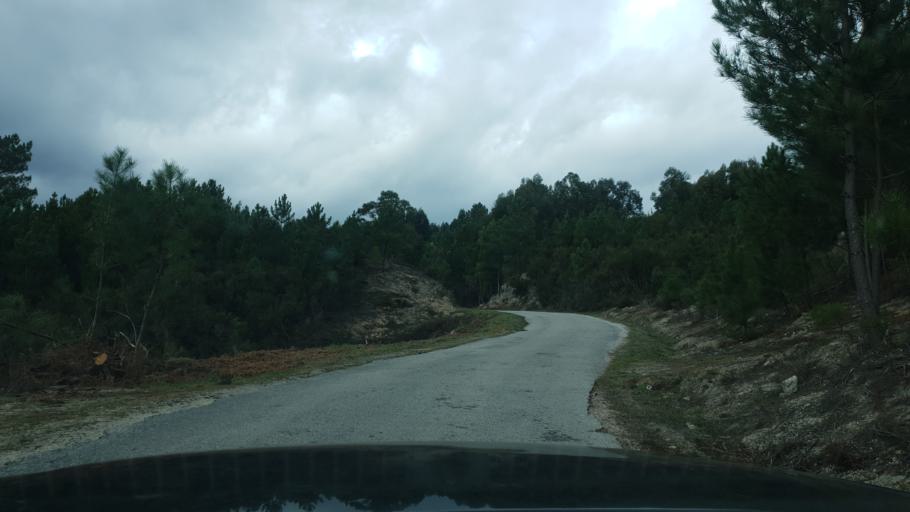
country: PT
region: Viseu
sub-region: Castro Daire
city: Castro Daire
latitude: 40.8791
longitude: -8.0010
